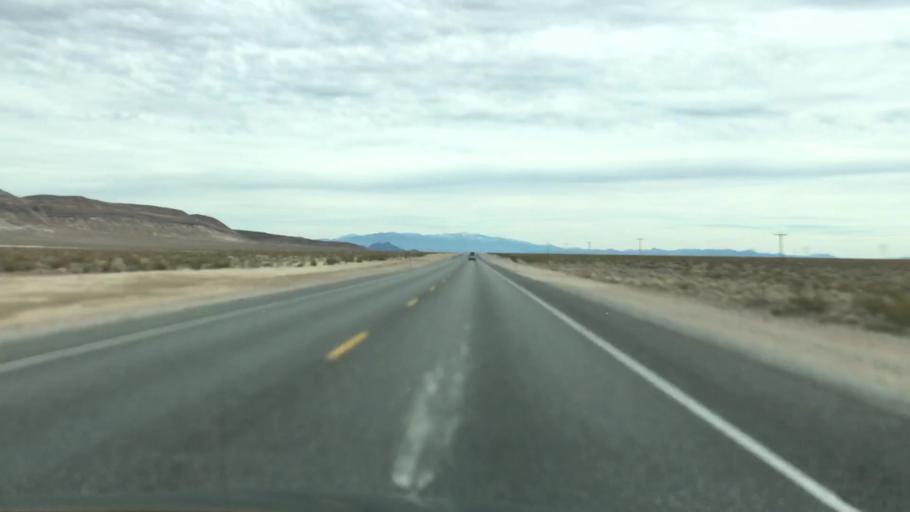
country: US
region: Nevada
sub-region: Nye County
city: Beatty
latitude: 36.6957
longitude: -116.5738
